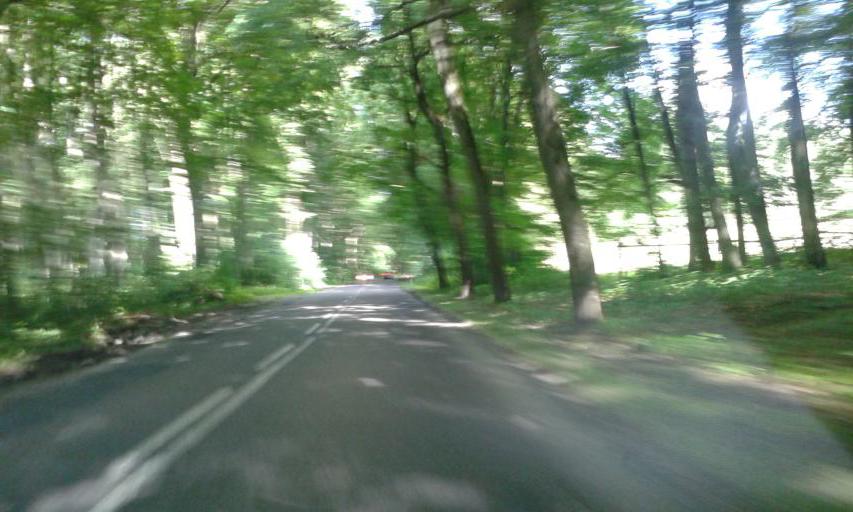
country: PL
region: West Pomeranian Voivodeship
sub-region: Powiat slawienski
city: Slawno
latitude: 54.2648
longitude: 16.6788
